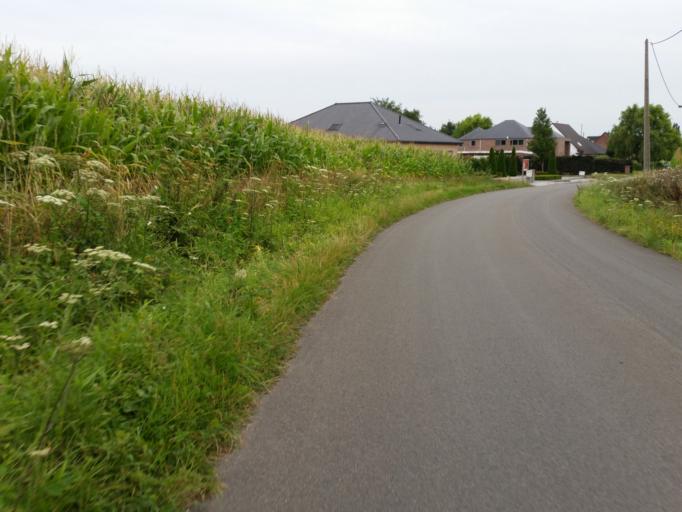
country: BE
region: Flanders
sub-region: Provincie Antwerpen
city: Rumst
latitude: 51.0876
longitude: 4.4482
